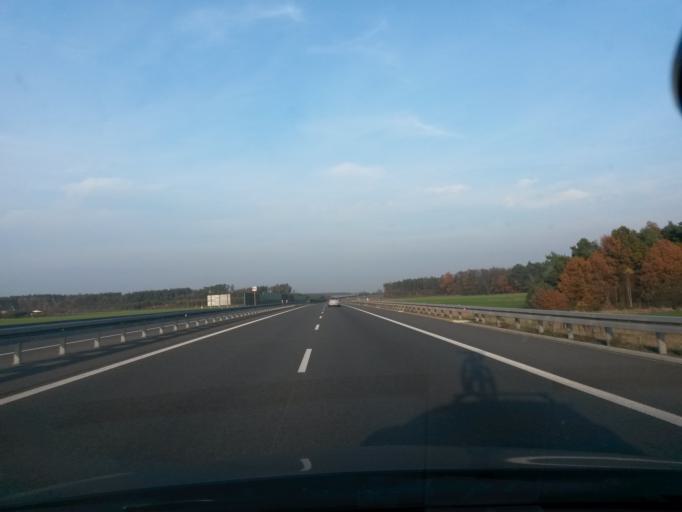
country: PL
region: Lower Silesian Voivodeship
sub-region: Powiat olesnicki
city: Twardogora
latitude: 51.2909
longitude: 17.5791
